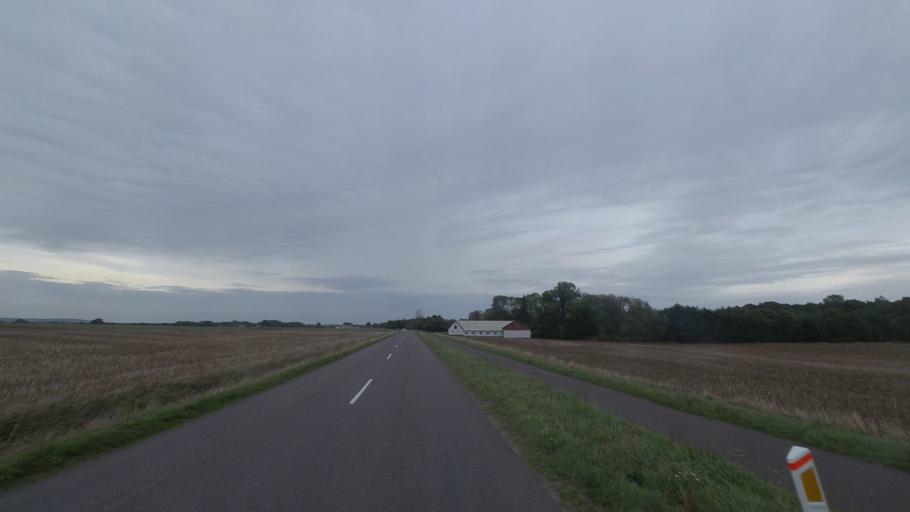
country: DK
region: Capital Region
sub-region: Bornholm Kommune
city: Nexo
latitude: 55.0055
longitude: 15.0885
